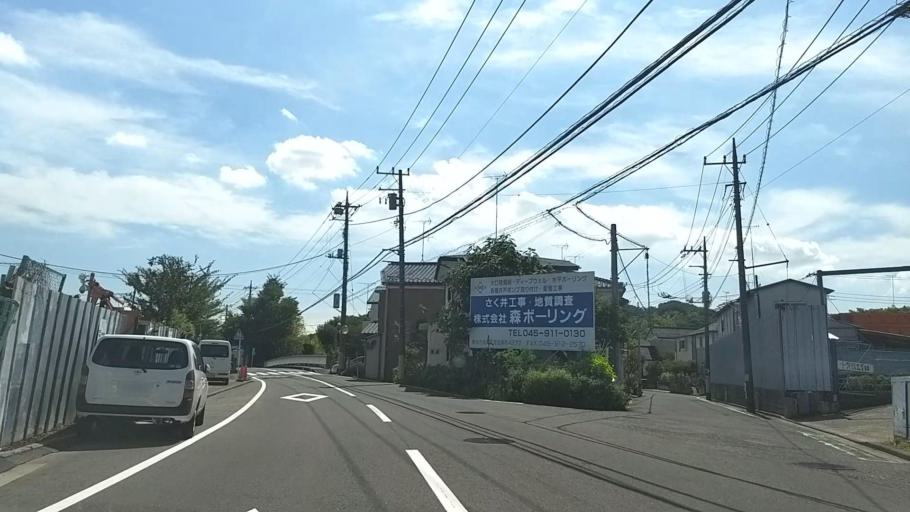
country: JP
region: Tokyo
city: Chofugaoka
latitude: 35.5545
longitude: 139.5674
